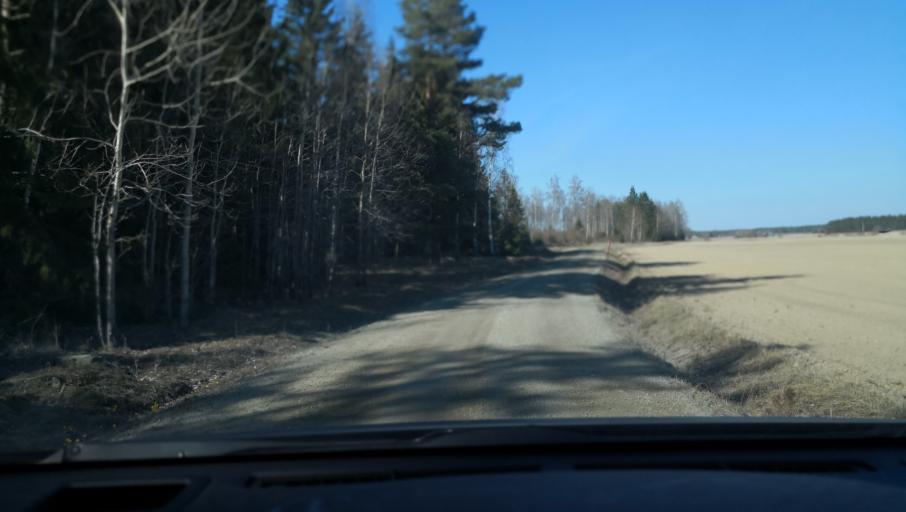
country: SE
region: Vaestmanland
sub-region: Sala Kommun
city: Sala
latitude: 59.8866
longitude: 16.5271
